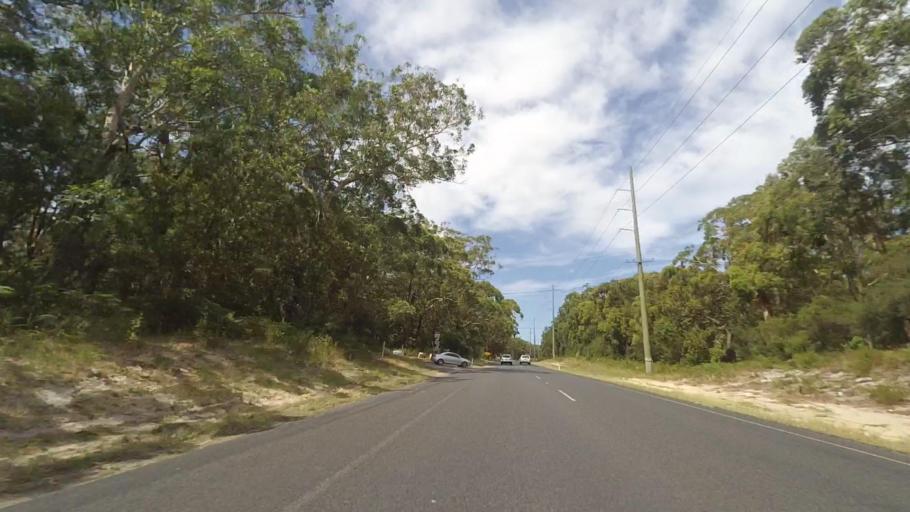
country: AU
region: New South Wales
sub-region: Port Stephens Shire
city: Anna Bay
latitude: -32.7821
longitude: 151.9826
